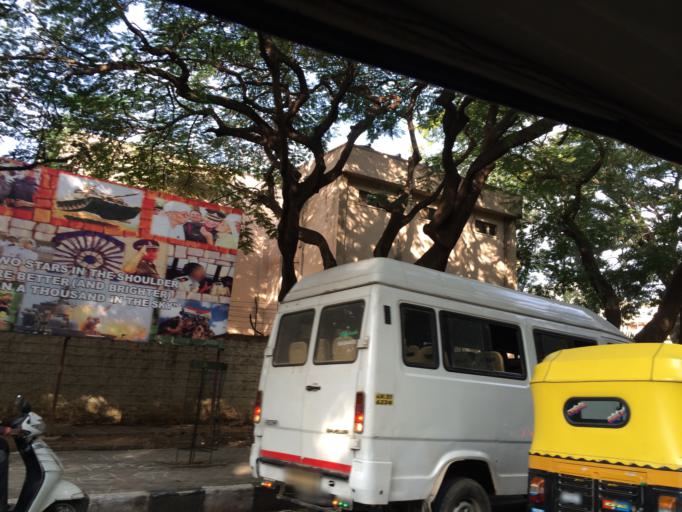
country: IN
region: Karnataka
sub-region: Bangalore Urban
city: Bangalore
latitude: 12.9756
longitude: 77.6138
